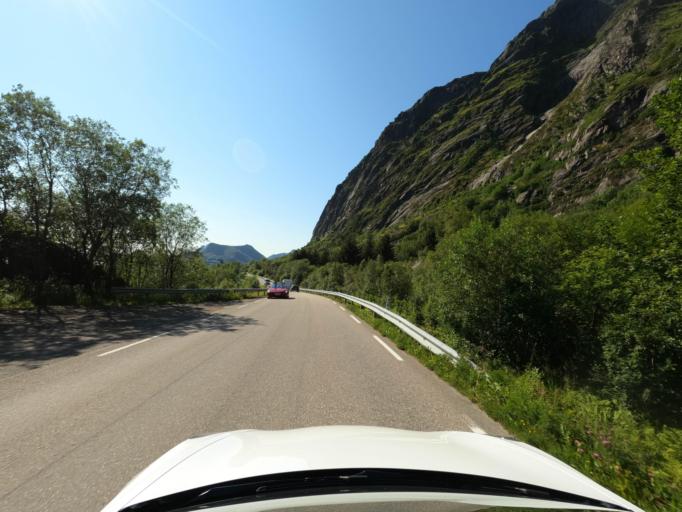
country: NO
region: Nordland
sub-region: Vagan
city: Svolvaer
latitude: 68.2443
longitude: 14.6101
